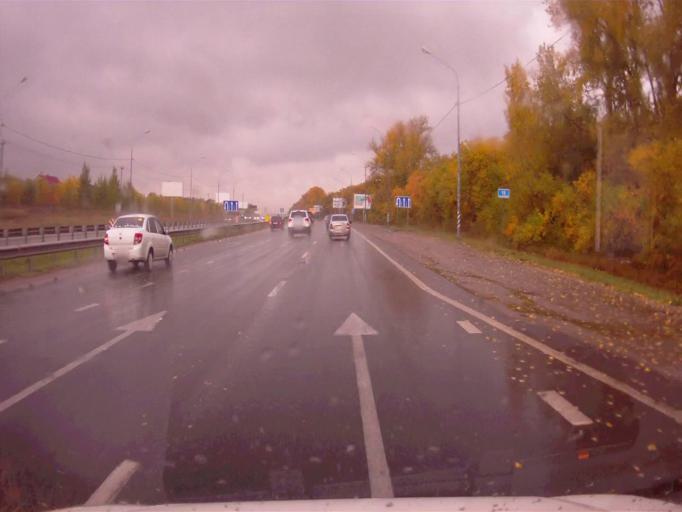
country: RU
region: Chelyabinsk
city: Dolgoderevenskoye
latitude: 55.2845
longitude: 61.3427
